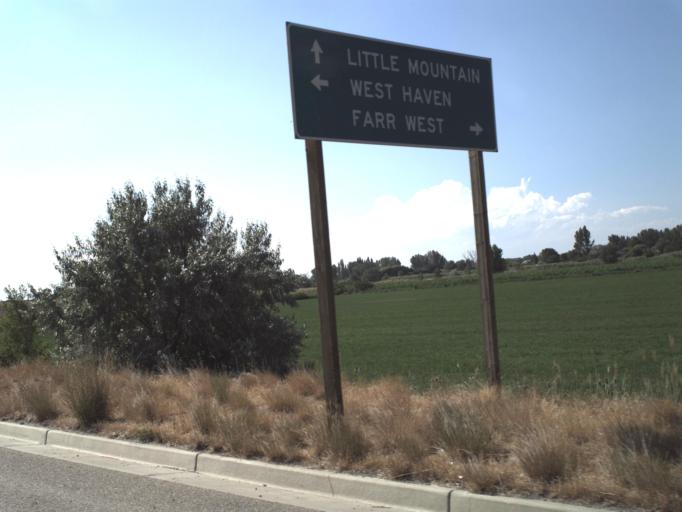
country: US
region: Utah
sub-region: Weber County
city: Marriott-Slaterville
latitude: 41.2448
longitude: -112.0189
